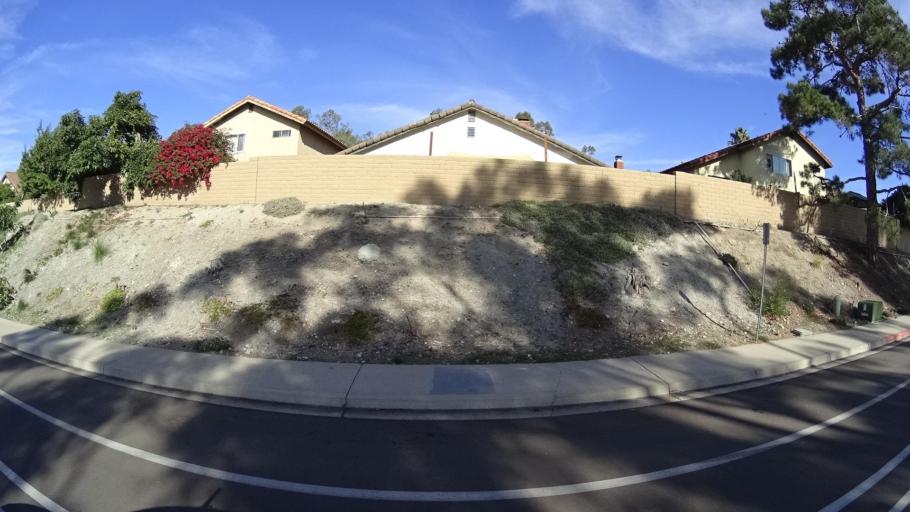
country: US
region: California
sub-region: San Diego County
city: Casa de Oro-Mount Helix
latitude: 32.7317
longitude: -116.9654
